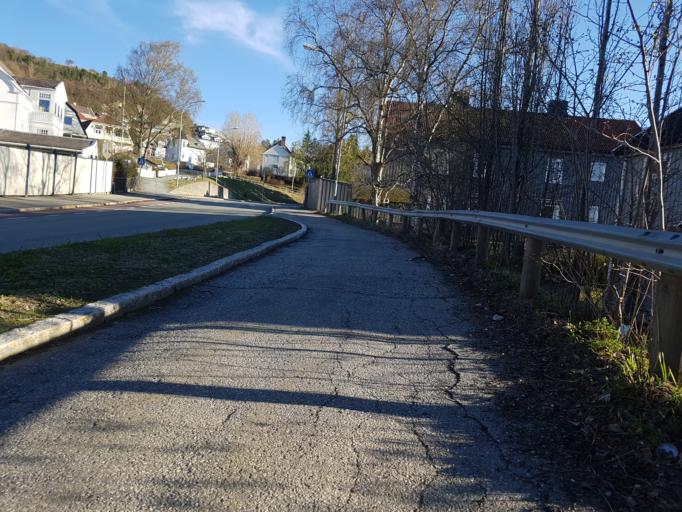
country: NO
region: Sor-Trondelag
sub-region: Trondheim
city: Trondheim
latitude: 63.4351
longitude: 10.4291
